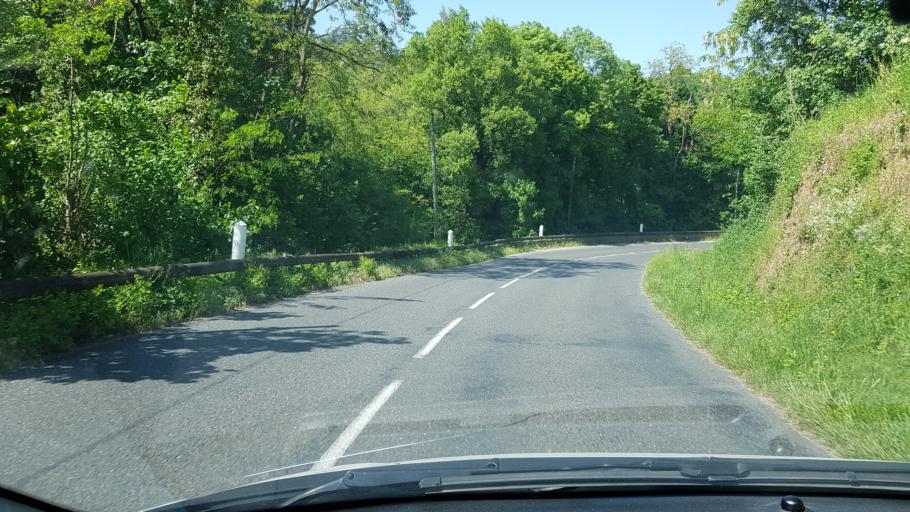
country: FR
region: Rhone-Alpes
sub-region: Departement du Rhone
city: Orlienas
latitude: 45.6599
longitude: 4.7216
